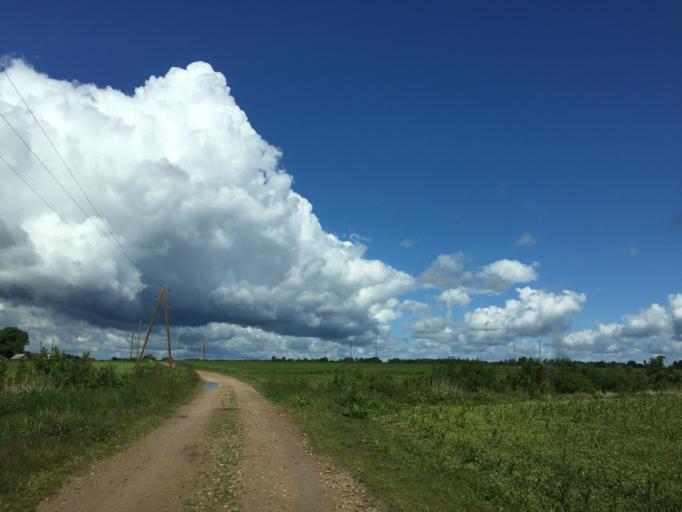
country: LV
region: Lecava
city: Iecava
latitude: 56.6161
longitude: 24.2074
